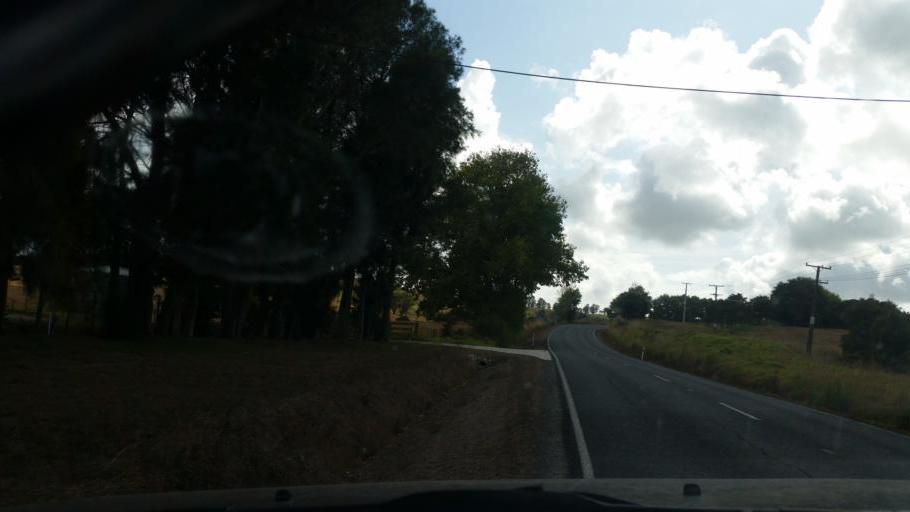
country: NZ
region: Auckland
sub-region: Auckland
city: Wellsford
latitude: -36.1372
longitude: 174.5168
